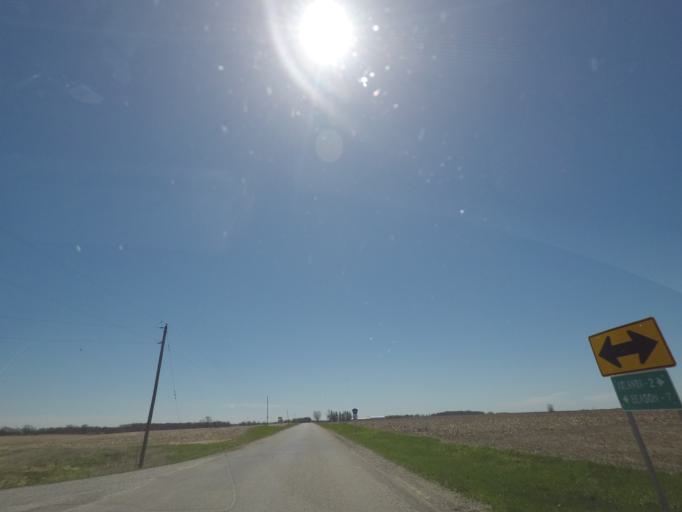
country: US
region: Illinois
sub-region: Logan County
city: Atlanta
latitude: 40.2434
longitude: -89.2050
